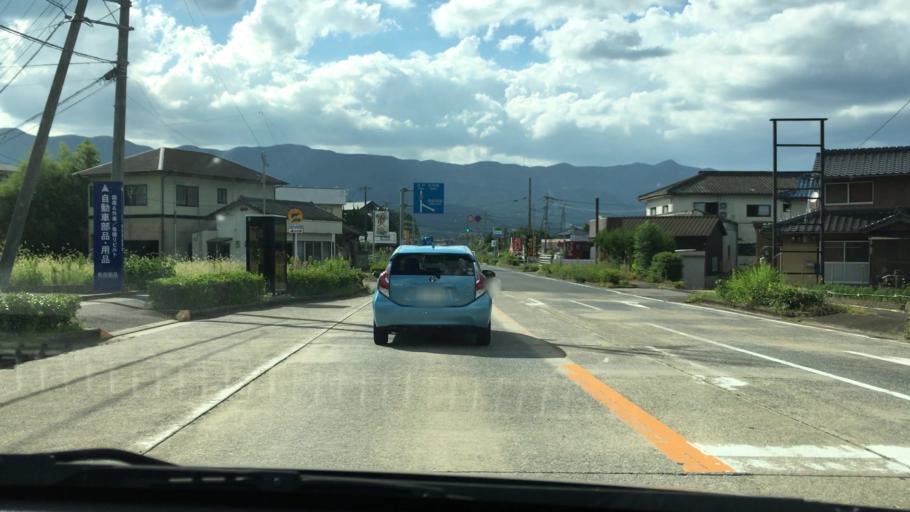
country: JP
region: Saga Prefecture
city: Imaricho-ko
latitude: 33.1864
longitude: 129.8675
